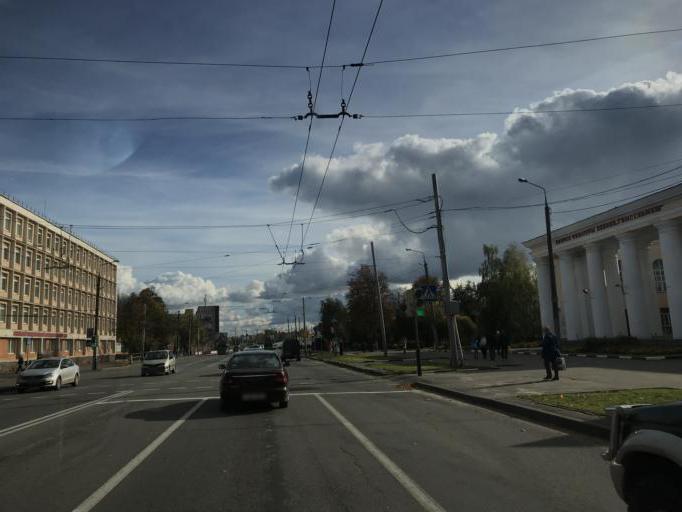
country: BY
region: Gomel
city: Gomel
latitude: 52.4489
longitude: 30.9683
